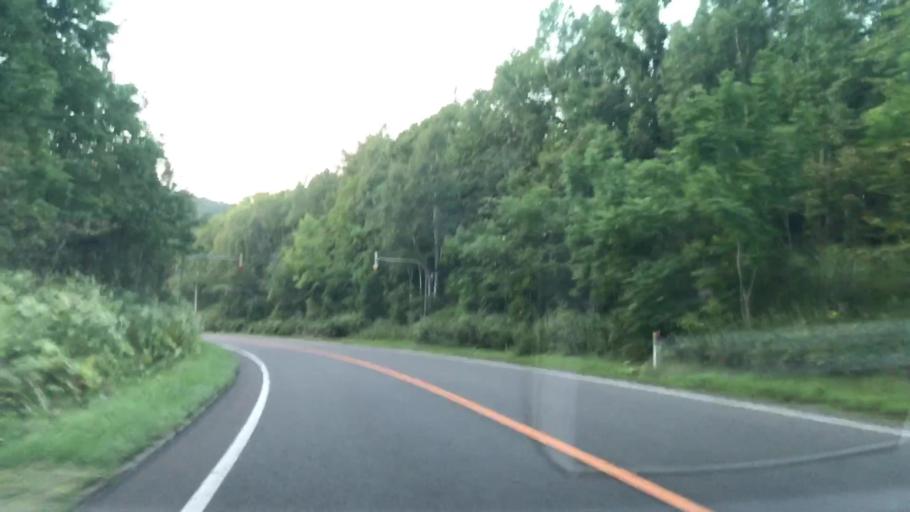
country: JP
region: Hokkaido
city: Sapporo
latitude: 42.9059
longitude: 141.1218
